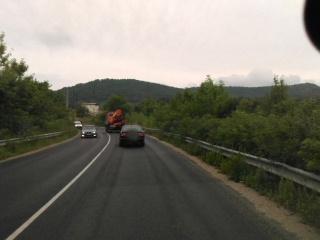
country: BG
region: Plovdiv
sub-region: Obshtina Karlovo
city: Karlovo
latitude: 42.5412
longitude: 24.8196
